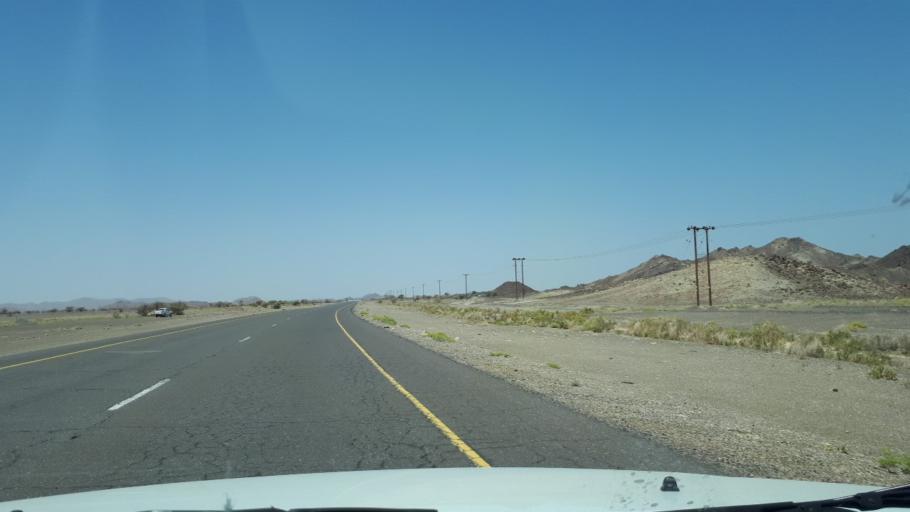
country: OM
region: Ash Sharqiyah
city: Ibra'
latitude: 22.6182
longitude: 58.4379
